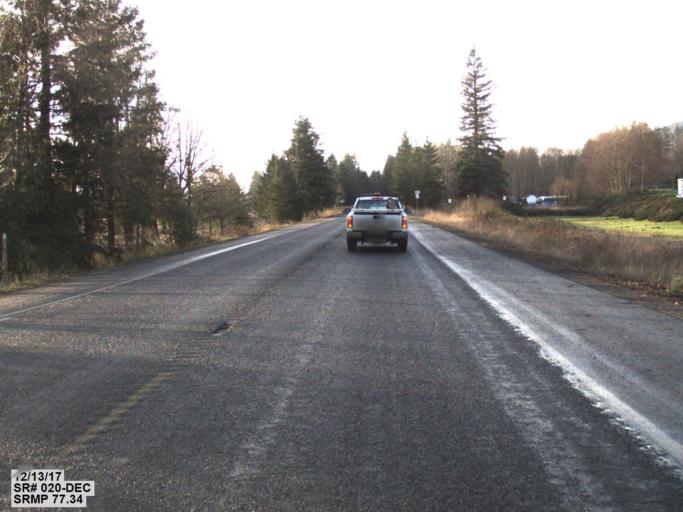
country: US
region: Washington
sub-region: Skagit County
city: Sedro-Woolley
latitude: 48.5298
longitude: -121.9915
